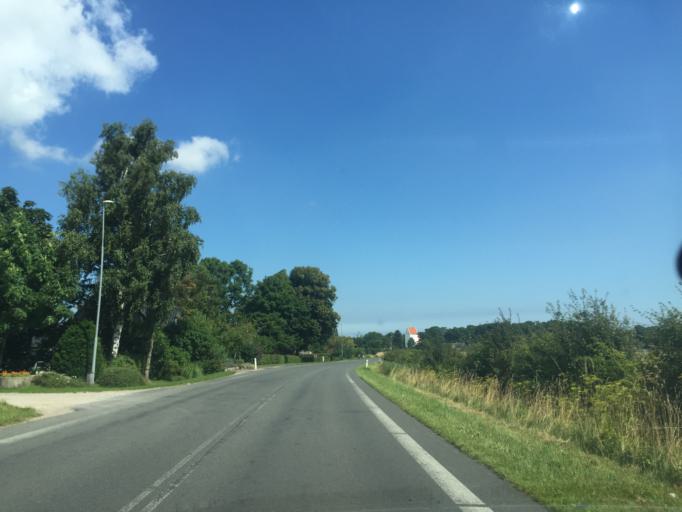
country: DK
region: South Denmark
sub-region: Nordfyns Kommune
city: Otterup
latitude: 55.5396
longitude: 10.3873
